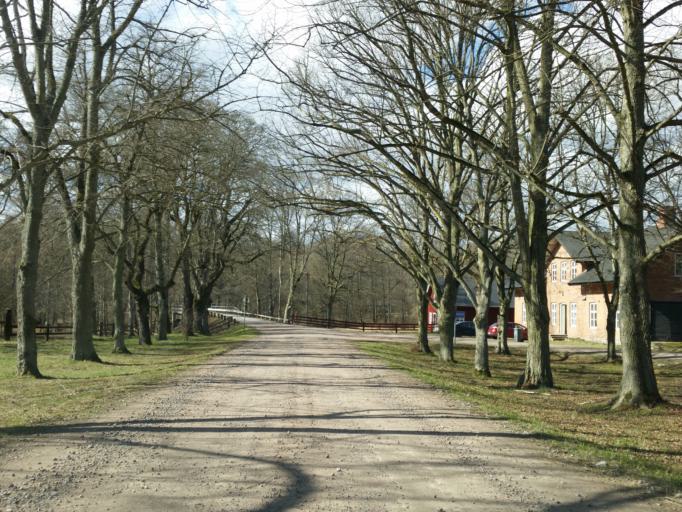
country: SE
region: Kalmar
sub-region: Monsteras Kommun
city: Timmernabben
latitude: 56.9365
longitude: 16.4241
